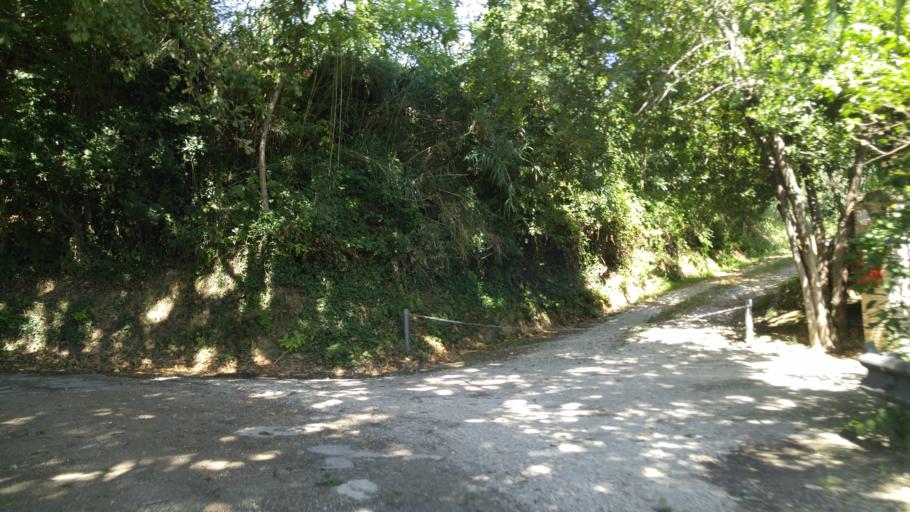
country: IT
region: The Marches
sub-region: Provincia di Pesaro e Urbino
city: Fenile
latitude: 43.8259
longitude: 12.9718
